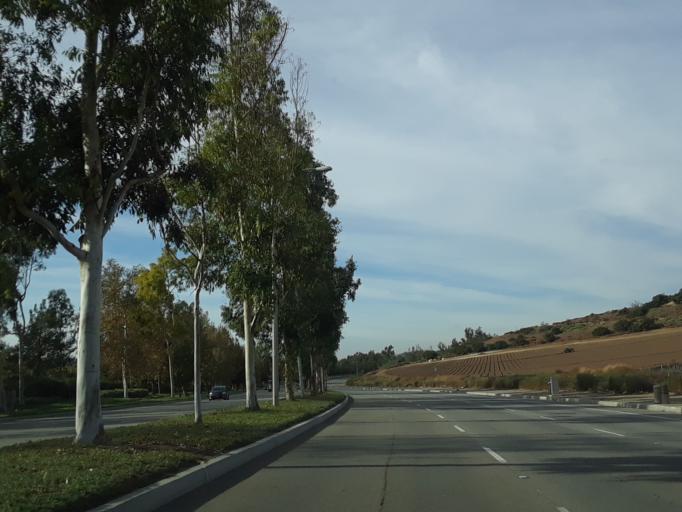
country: US
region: California
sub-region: Orange County
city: North Tustin
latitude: 33.7211
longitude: -117.7417
